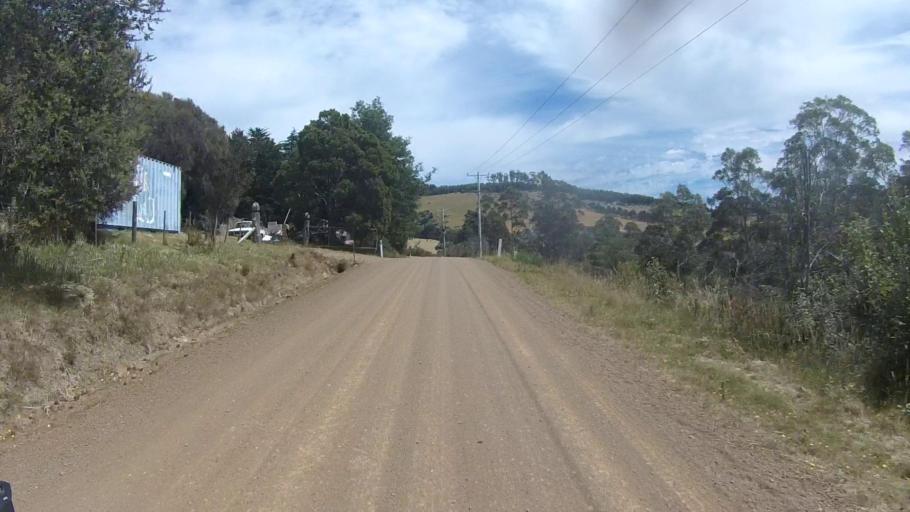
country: AU
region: Tasmania
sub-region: Sorell
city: Sorell
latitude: -42.7902
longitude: 147.8451
